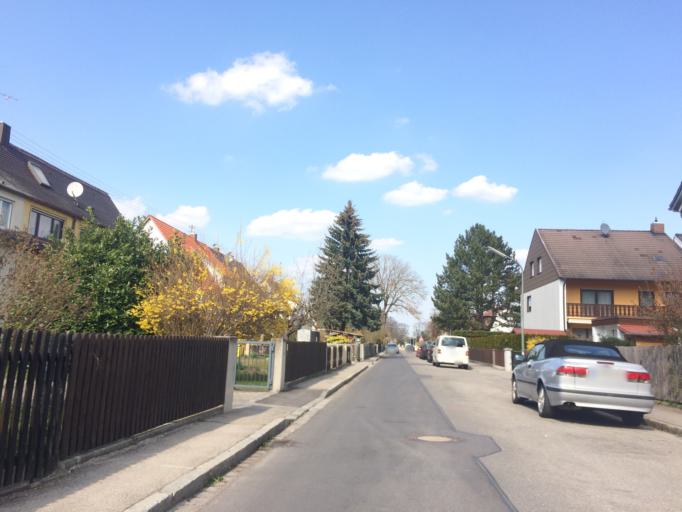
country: DE
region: Bavaria
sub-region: Swabia
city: Gersthofen
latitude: 48.4080
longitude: 10.8967
